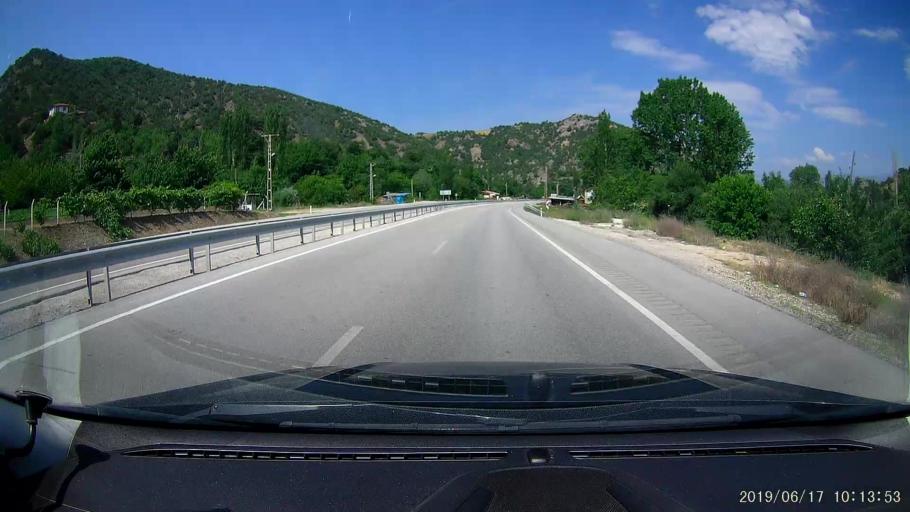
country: TR
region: Amasya
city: Saraycik
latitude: 40.9864
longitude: 35.0374
